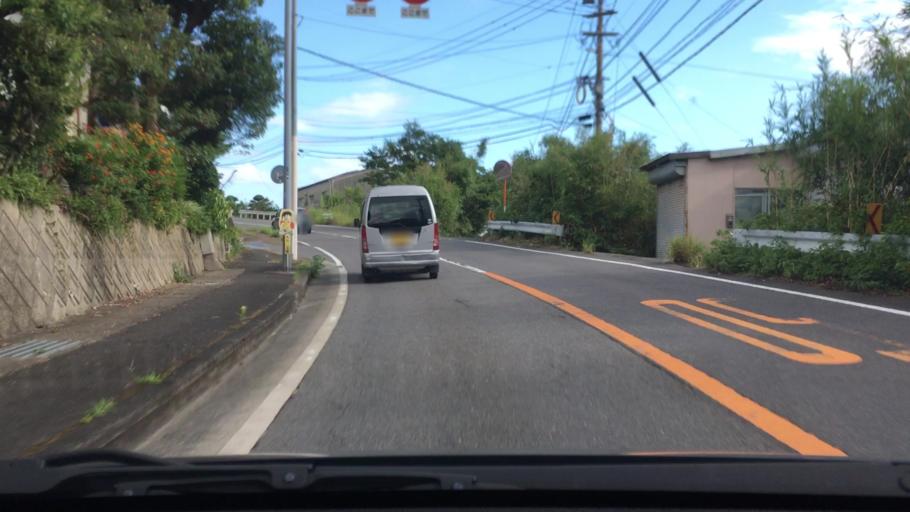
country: JP
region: Nagasaki
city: Togitsu
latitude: 32.8215
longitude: 129.7343
